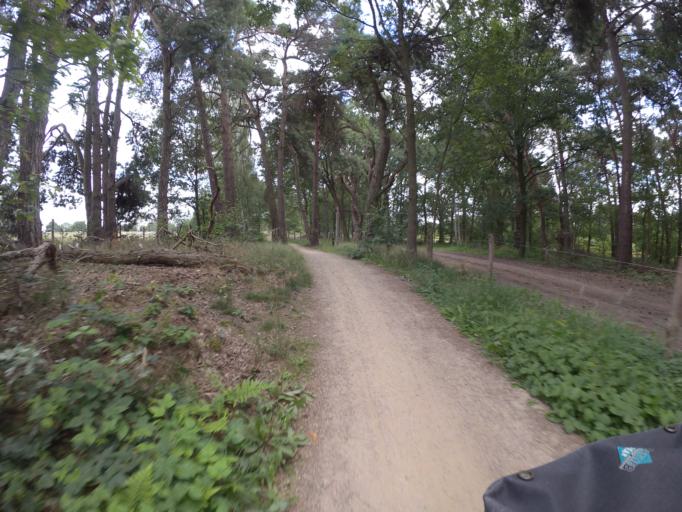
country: NL
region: North Brabant
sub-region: Gemeente Heeze-Leende
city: Heeze
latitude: 51.4015
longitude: 5.5845
